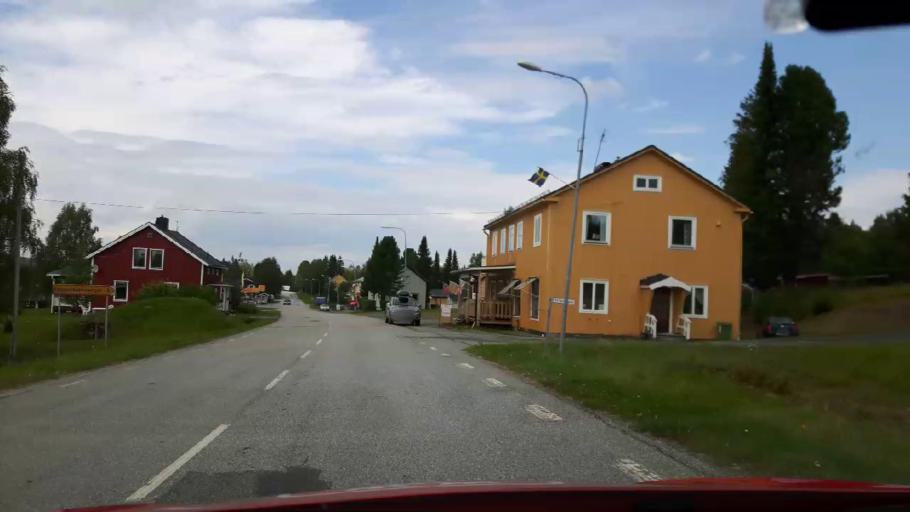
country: SE
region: Jaemtland
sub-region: Stroemsunds Kommun
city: Stroemsund
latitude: 64.4340
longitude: 15.5949
